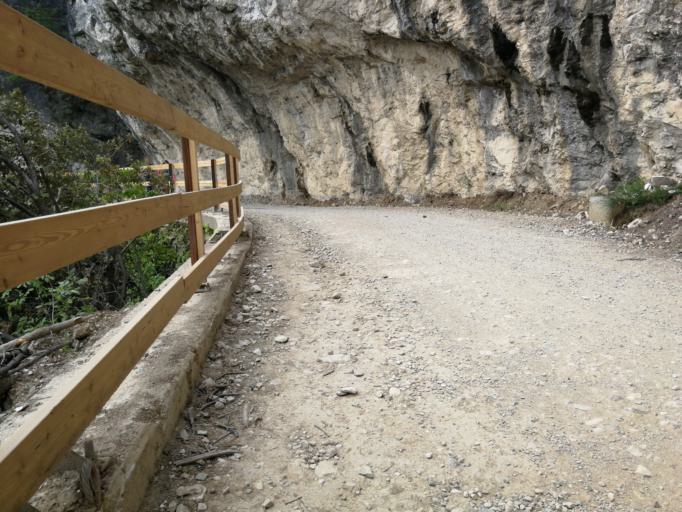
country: IT
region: Trentino-Alto Adige
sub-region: Provincia di Trento
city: Riva del Garda
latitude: 45.8762
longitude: 10.8384
